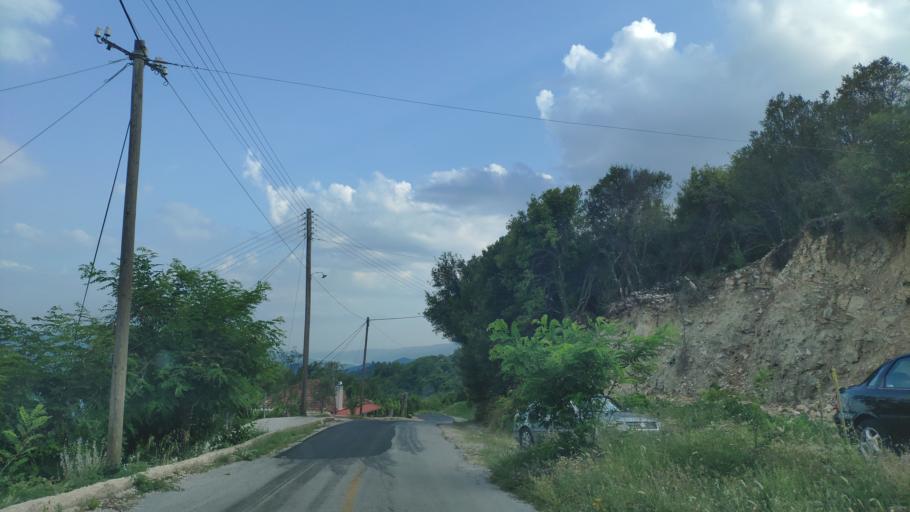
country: GR
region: Epirus
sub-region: Nomos Artas
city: Agios Dimitrios
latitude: 39.3729
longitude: 21.0248
